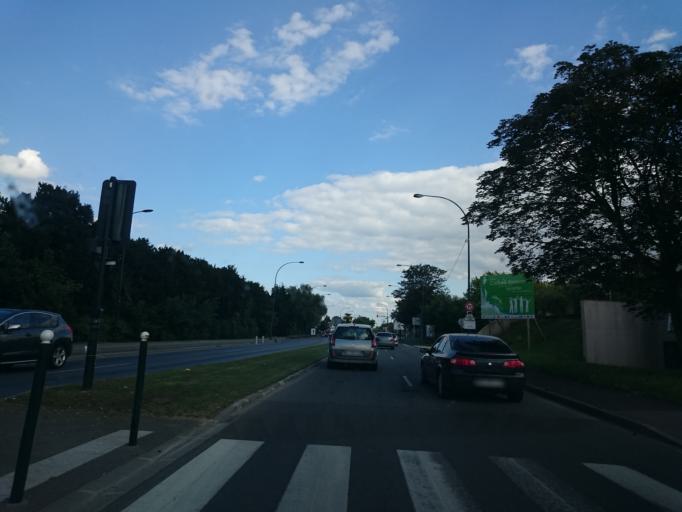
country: FR
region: Ile-de-France
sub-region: Departement de l'Essonne
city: Evry
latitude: 48.6154
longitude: 2.4568
